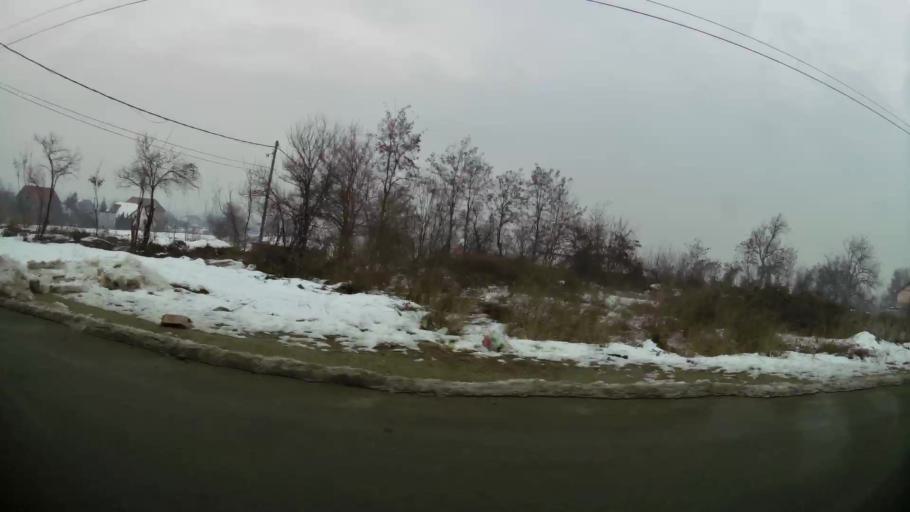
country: MK
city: Kondovo
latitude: 42.0486
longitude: 21.3472
